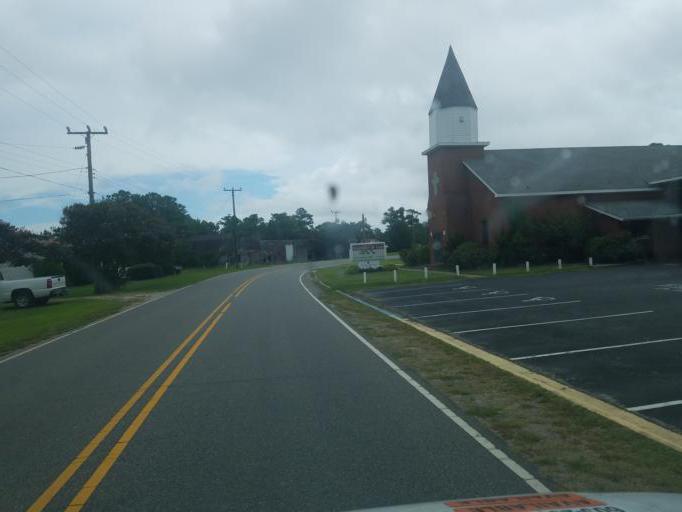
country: US
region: North Carolina
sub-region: Dare County
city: Wanchese
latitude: 35.8430
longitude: -75.6271
